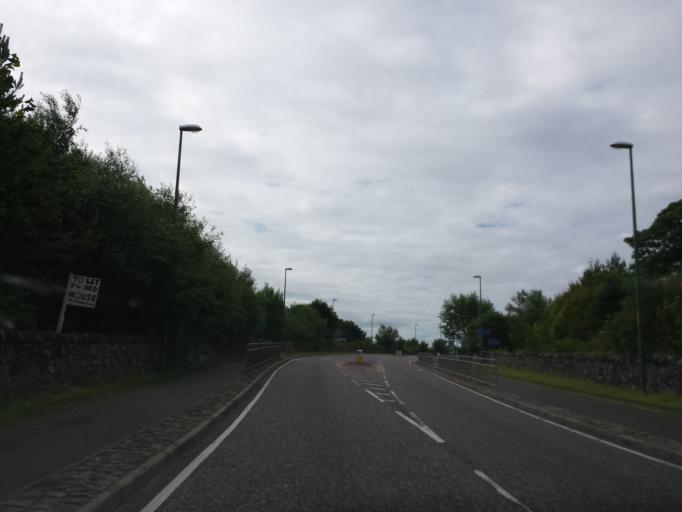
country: GB
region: Scotland
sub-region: Argyll and Bute
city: Isle Of Mull
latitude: 56.9116
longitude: -5.8409
